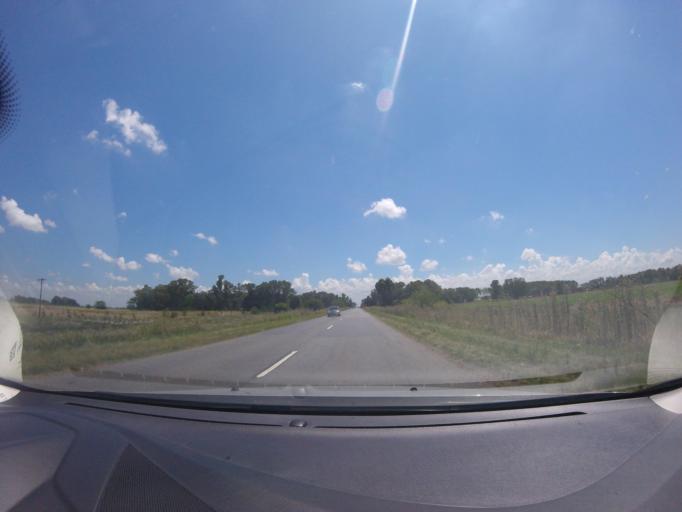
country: AR
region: Buenos Aires
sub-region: Partido de Las Flores
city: Las Flores
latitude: -36.2218
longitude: -59.0447
